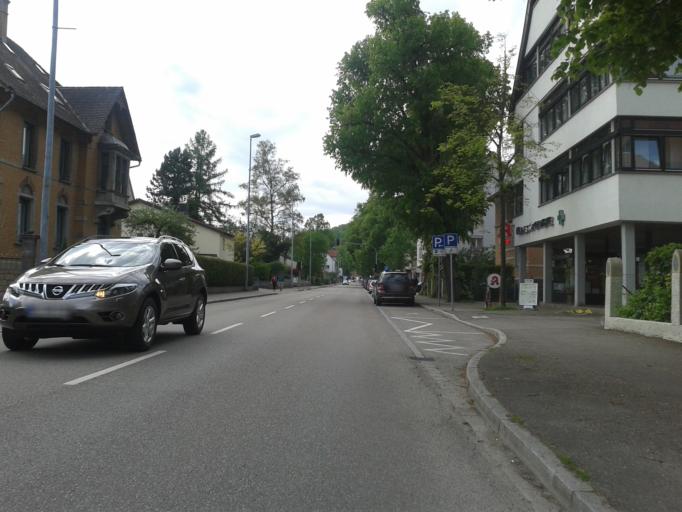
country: DE
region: Baden-Wuerttemberg
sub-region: Tuebingen Region
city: Blaubeuren
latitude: 48.4081
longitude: 9.7875
